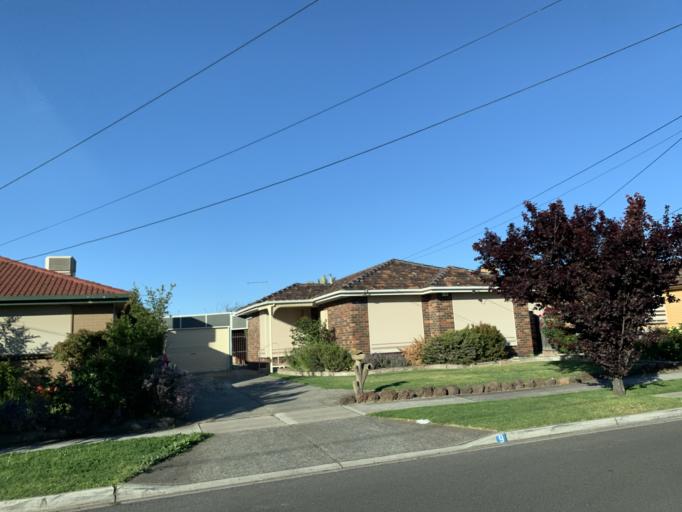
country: AU
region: Victoria
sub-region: Brimbank
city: Sunshine North
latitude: -37.7581
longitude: 144.8148
